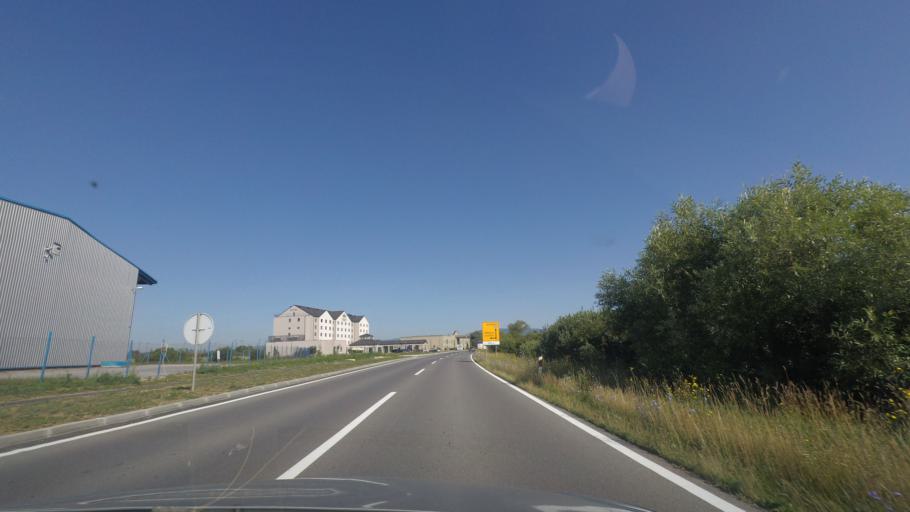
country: HR
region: Zagrebacka
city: Jastrebarsko
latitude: 45.6527
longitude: 15.6587
